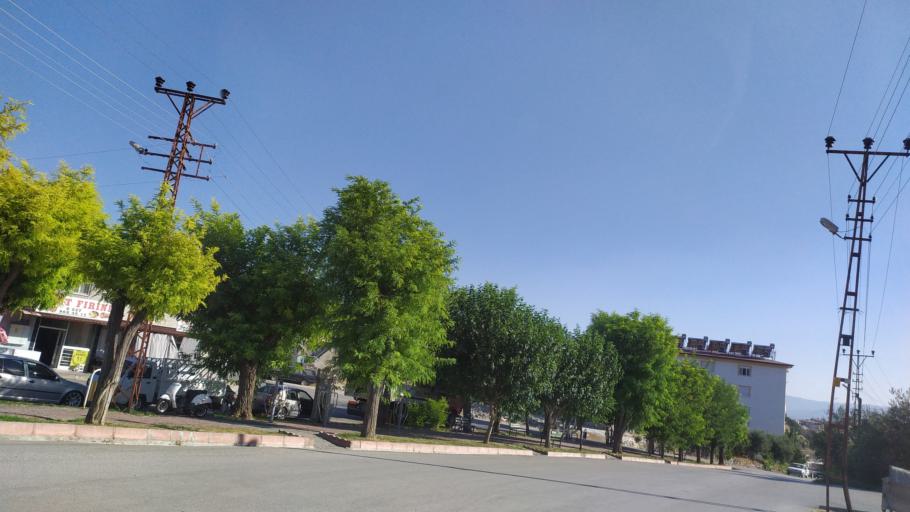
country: TR
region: Mersin
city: Mut
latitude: 36.6492
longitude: 33.4348
